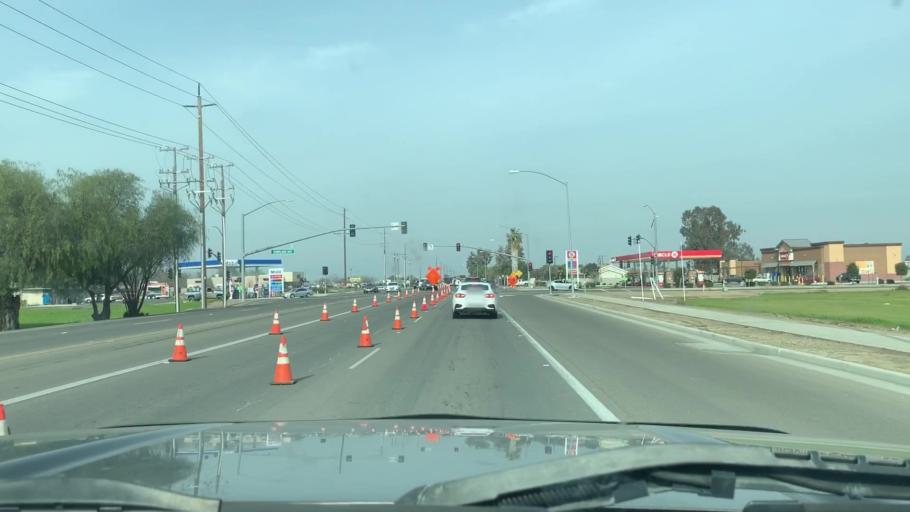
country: US
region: California
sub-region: Merced County
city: Los Banos
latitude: 37.0729
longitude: -120.8350
